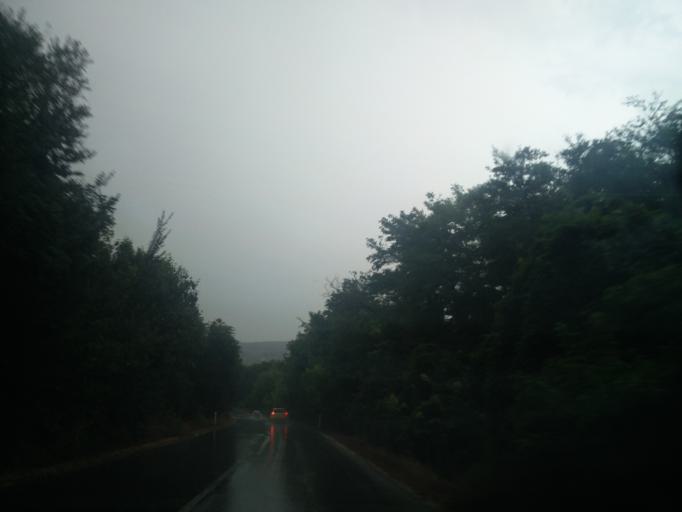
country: HU
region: Pest
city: Biatorbagy
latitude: 47.4564
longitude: 18.8039
